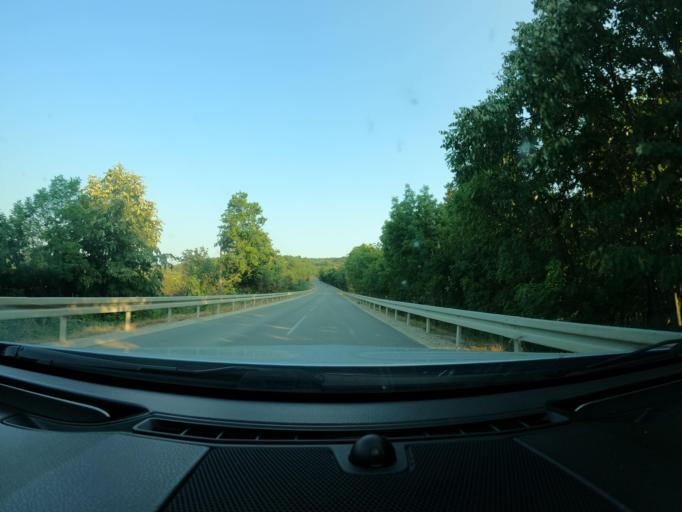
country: RS
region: Autonomna Pokrajina Vojvodina
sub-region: Juznobacki Okrug
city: Beocin
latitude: 45.1661
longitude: 19.7132
